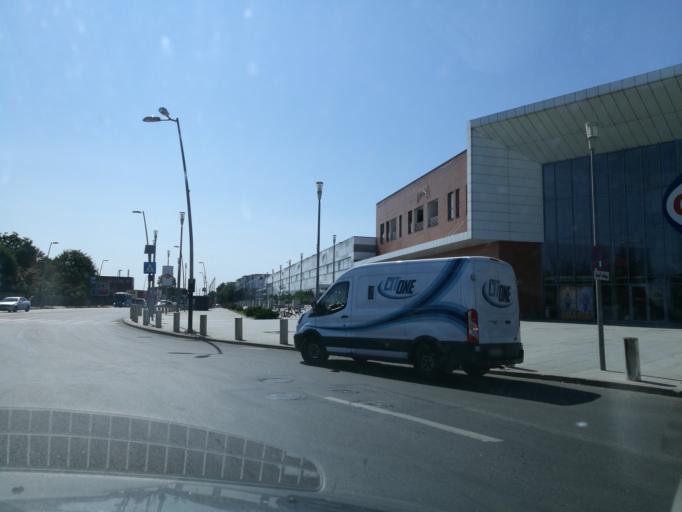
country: RO
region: Bacau
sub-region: Municipiul Bacau
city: Bacau
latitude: 46.5633
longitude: 26.9229
